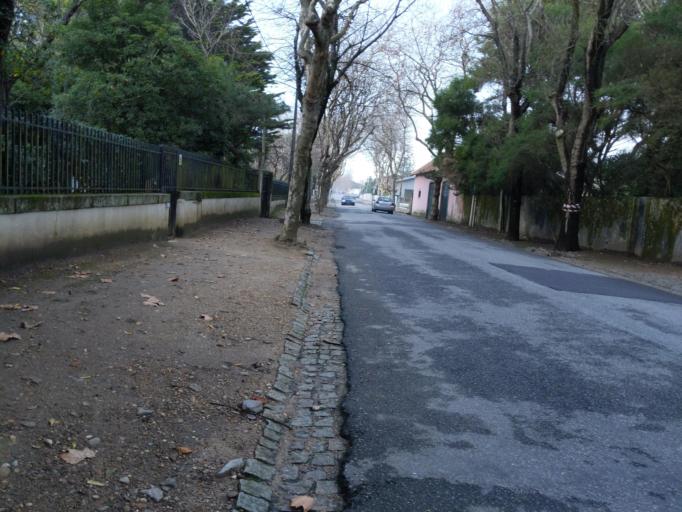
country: PT
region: Porto
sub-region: Vila Nova de Gaia
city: Arcozelo
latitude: 41.0425
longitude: -8.6496
